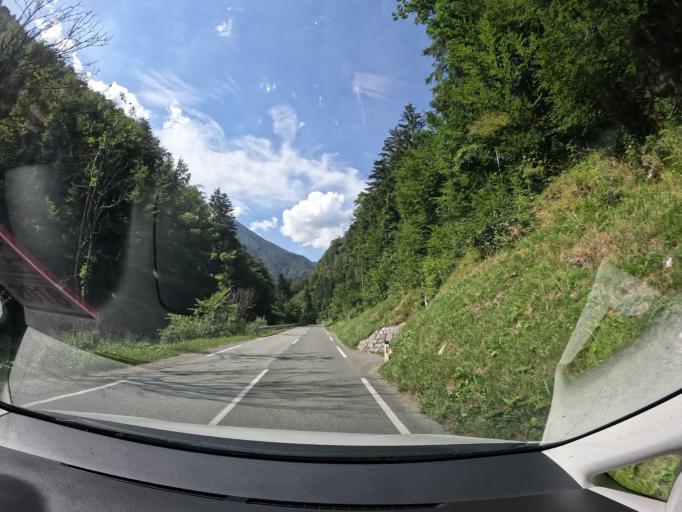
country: SI
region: Jezersko
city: Zgornje Jezersko
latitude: 46.3580
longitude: 14.4633
